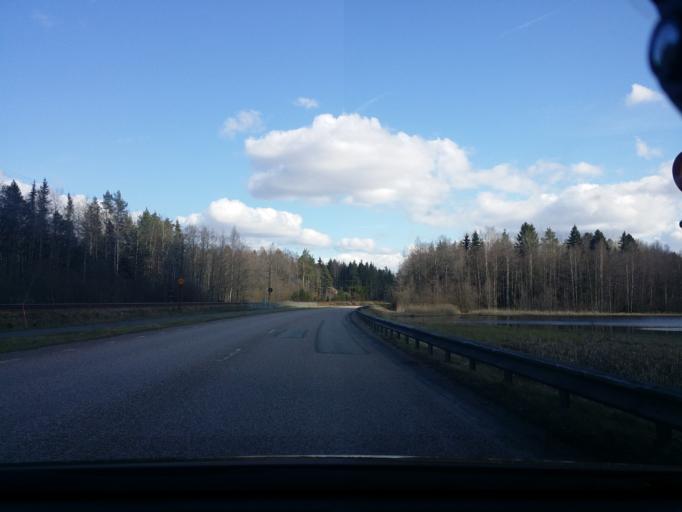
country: SE
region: Vaestmanland
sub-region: Sala Kommun
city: Sala
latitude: 59.9468
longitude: 16.5438
